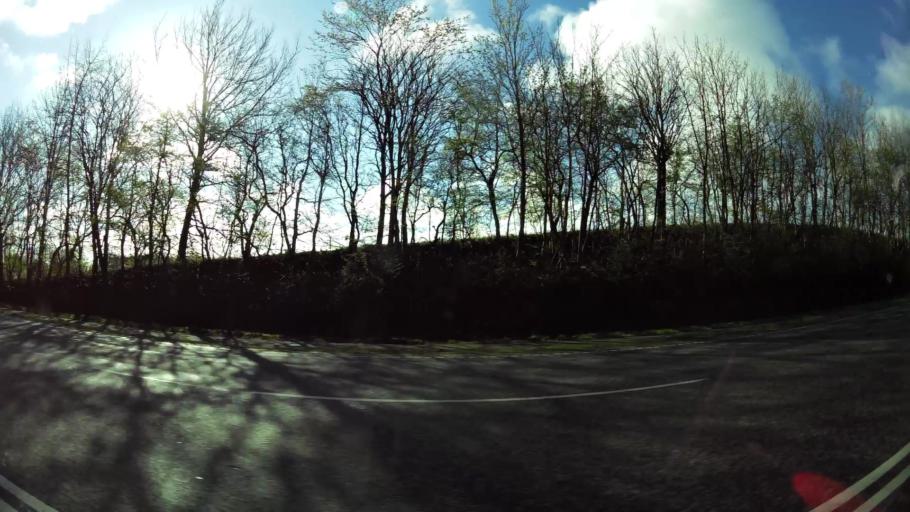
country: DK
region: Zealand
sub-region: Lejre Kommune
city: Kirke Hvalso
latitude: 55.4966
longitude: 11.8715
